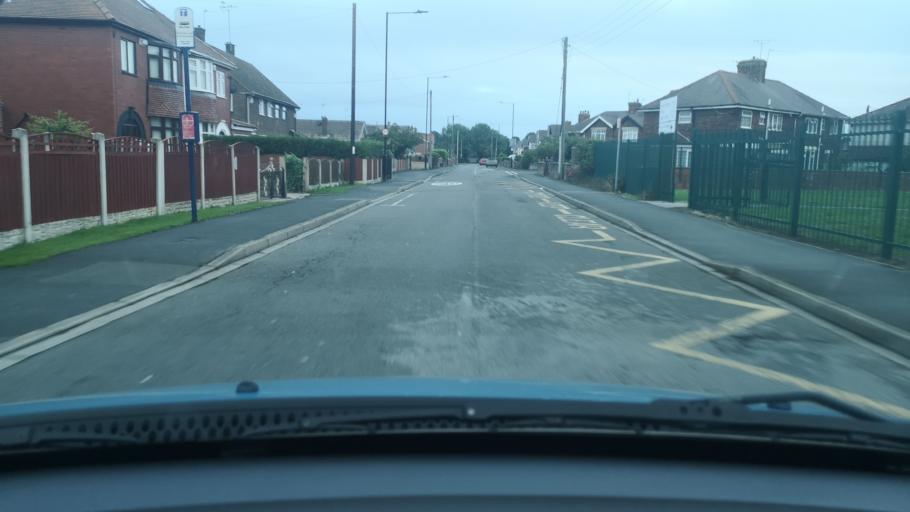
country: GB
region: England
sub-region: Doncaster
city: Askern
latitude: 53.6158
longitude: -1.1417
